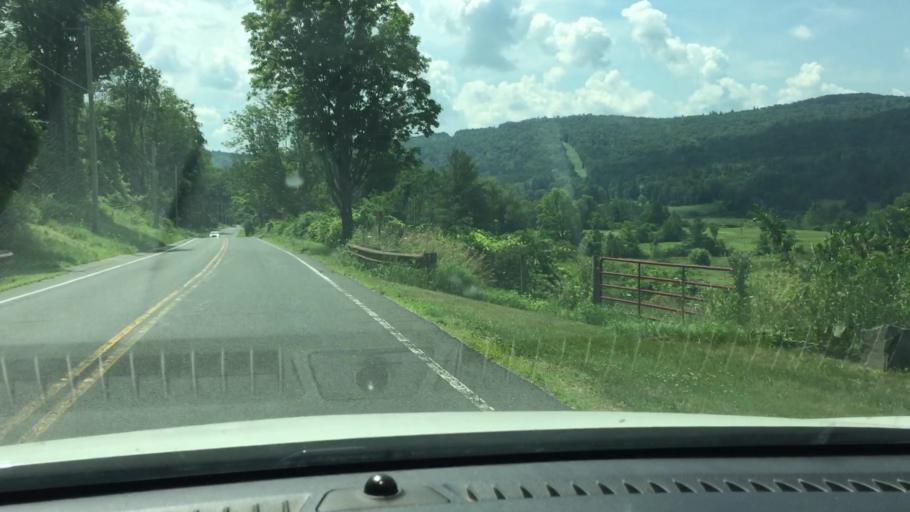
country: US
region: Massachusetts
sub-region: Berkshire County
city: Lee
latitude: 42.2273
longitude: -73.1882
